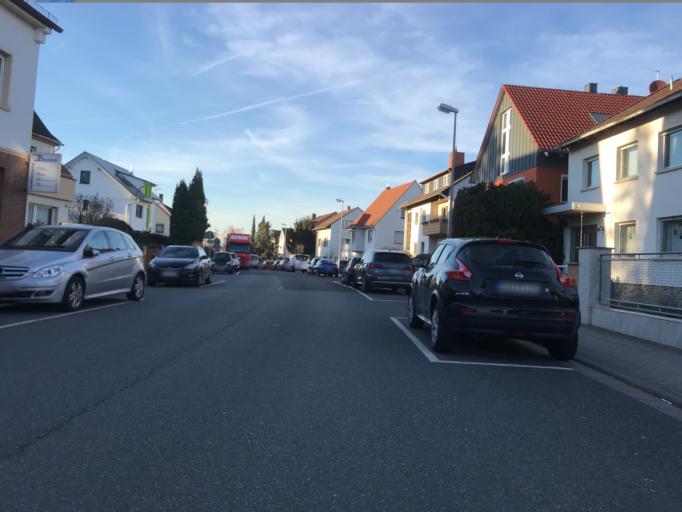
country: DE
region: Rheinland-Pfalz
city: Mainz
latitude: 49.9644
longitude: 8.2782
